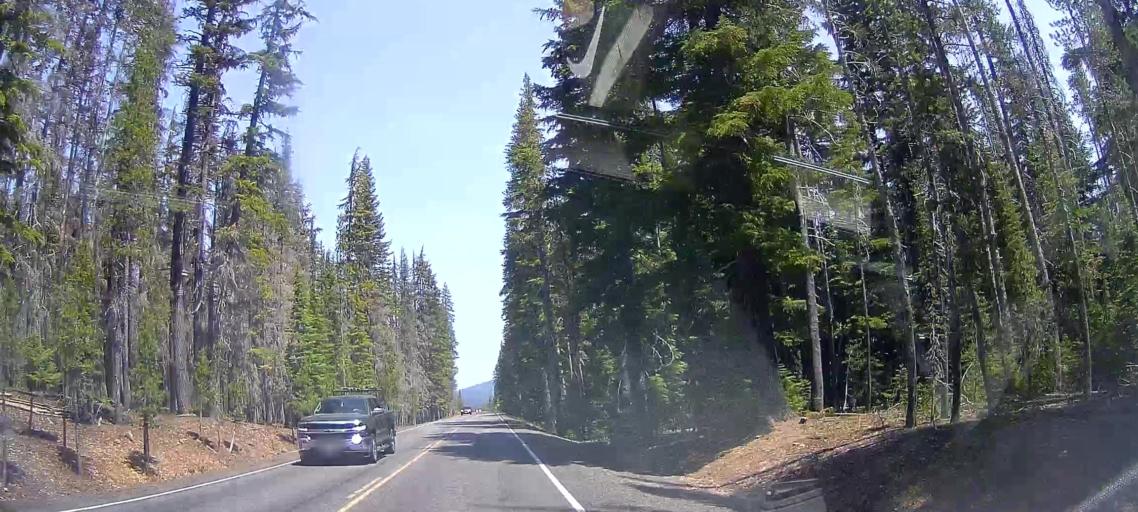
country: US
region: Oregon
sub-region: Lane County
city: Oakridge
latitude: 43.0653
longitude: -122.1202
